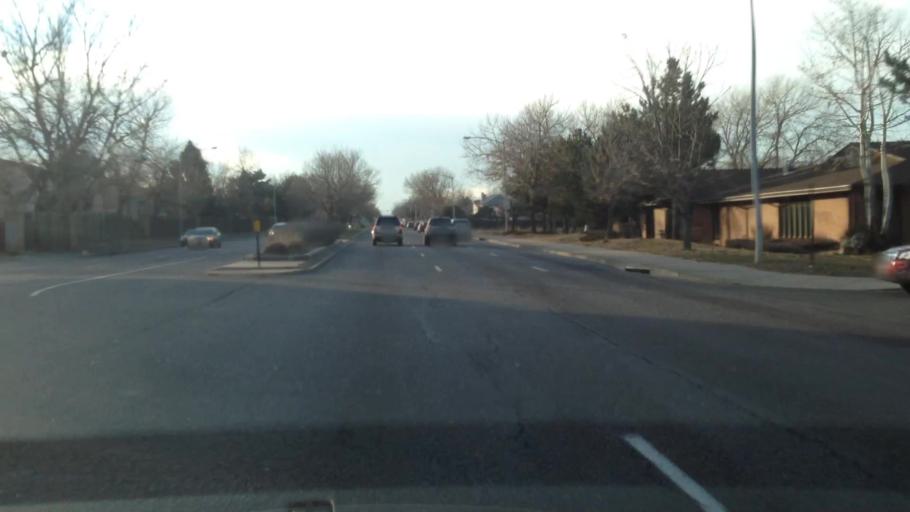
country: US
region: Colorado
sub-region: Adams County
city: Aurora
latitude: 39.6749
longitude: -104.8121
